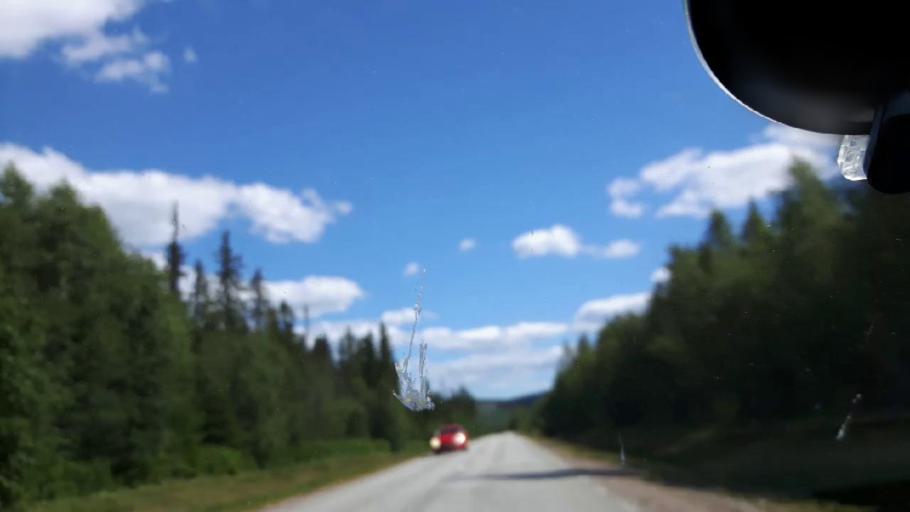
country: SE
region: Jaemtland
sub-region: Ragunda Kommun
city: Hammarstrand
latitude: 62.9605
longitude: 16.1769
